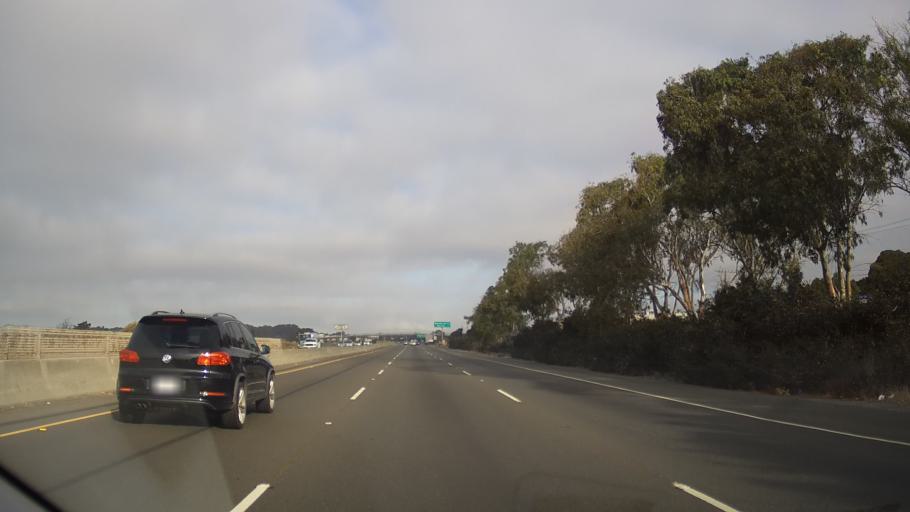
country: US
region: California
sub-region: Contra Costa County
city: El Cerrito
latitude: 37.9042
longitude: -122.3173
